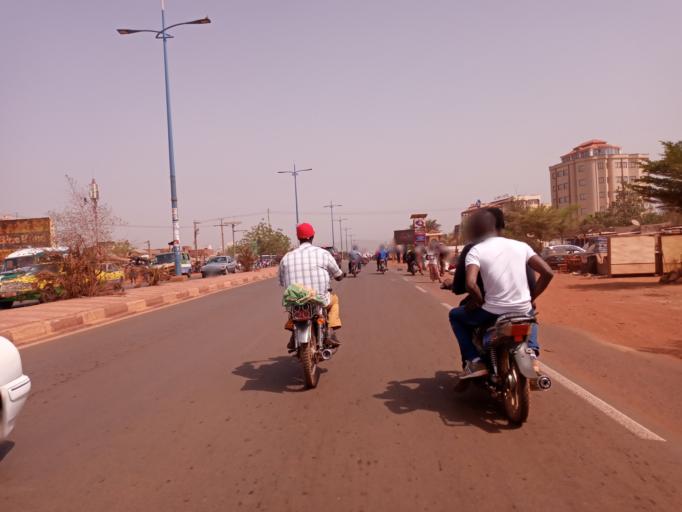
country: ML
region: Bamako
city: Bamako
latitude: 12.6018
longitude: -7.9937
